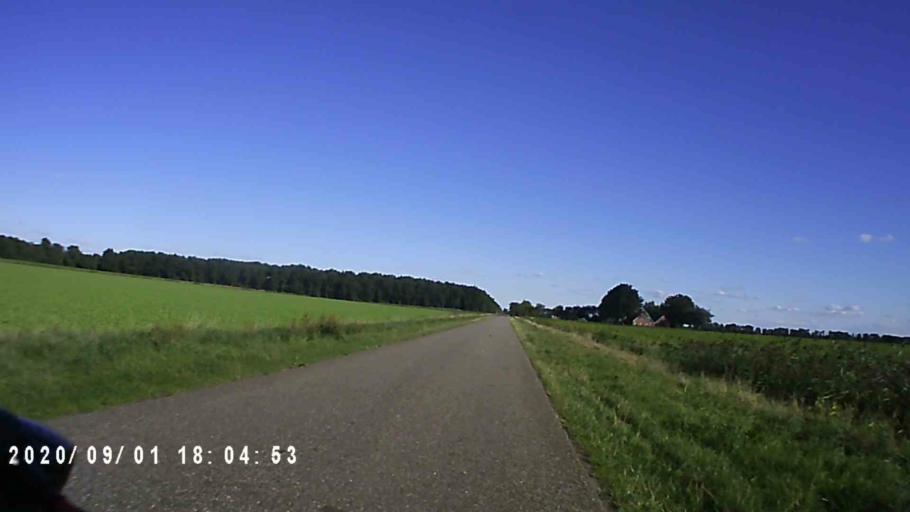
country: NL
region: Groningen
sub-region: Gemeente Slochteren
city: Slochteren
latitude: 53.1994
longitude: 6.7928
